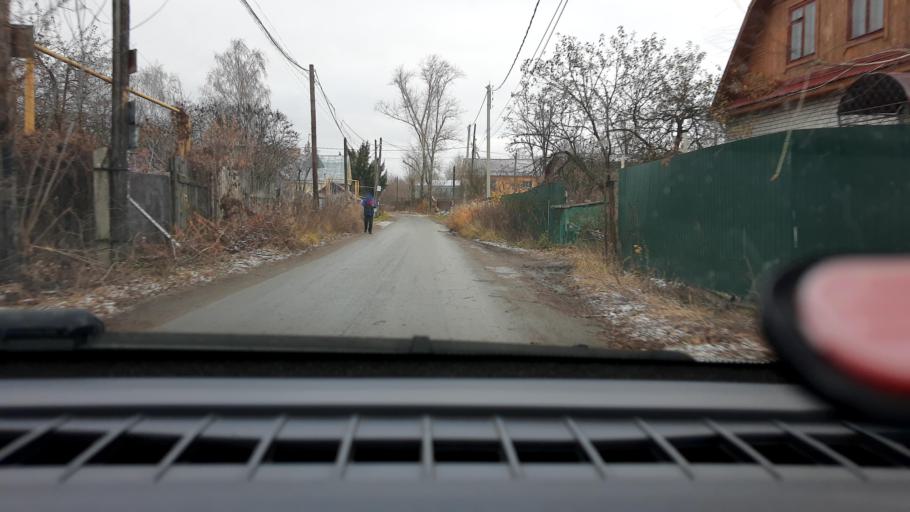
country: RU
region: Nizjnij Novgorod
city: Burevestnik
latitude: 56.2027
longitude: 43.7929
